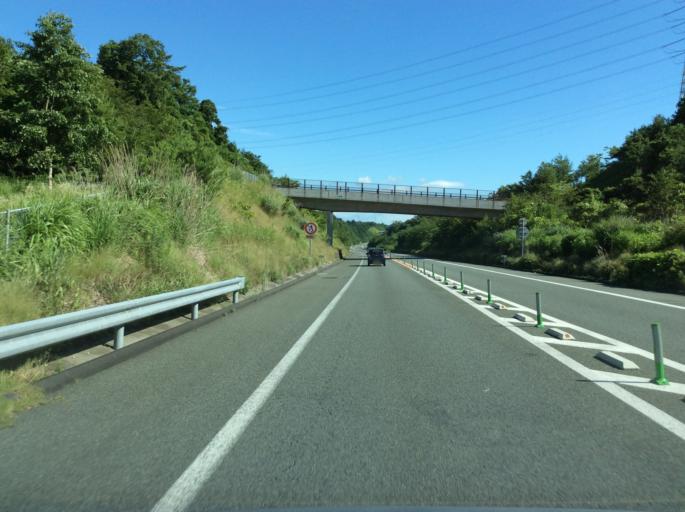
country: JP
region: Fukushima
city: Namie
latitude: 37.3159
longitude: 140.9924
